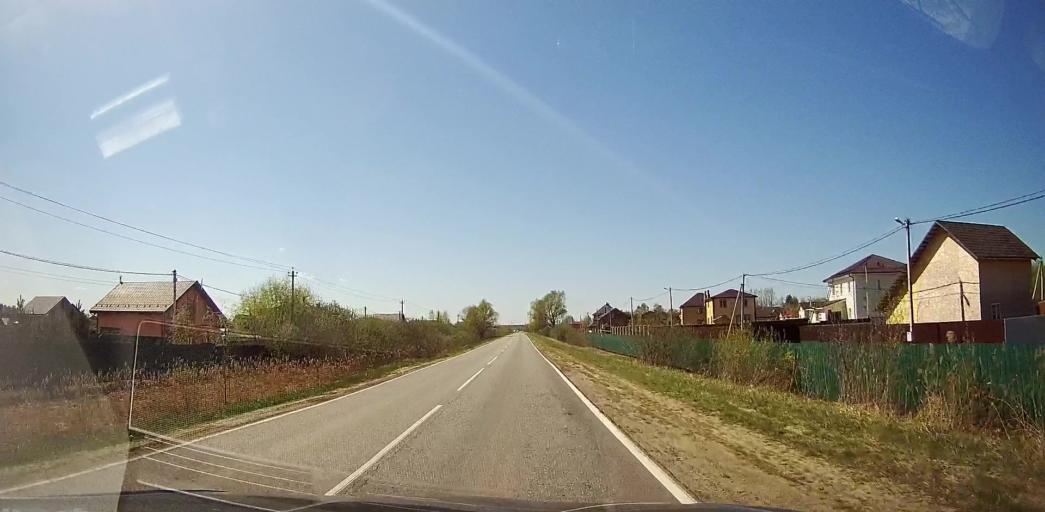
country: RU
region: Moskovskaya
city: Bronnitsy
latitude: 55.4562
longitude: 38.2796
